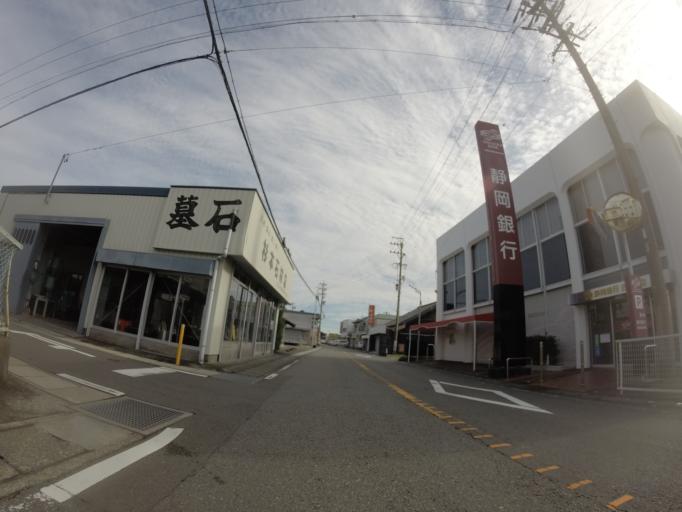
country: JP
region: Shizuoka
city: Sagara
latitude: 34.7580
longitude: 138.2542
